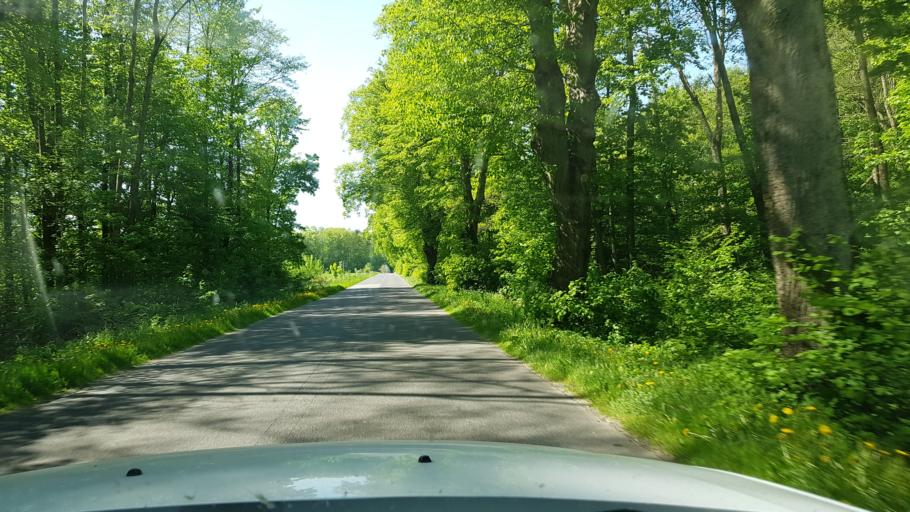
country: PL
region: West Pomeranian Voivodeship
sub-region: Powiat bialogardzki
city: Karlino
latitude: 54.0411
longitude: 15.7900
